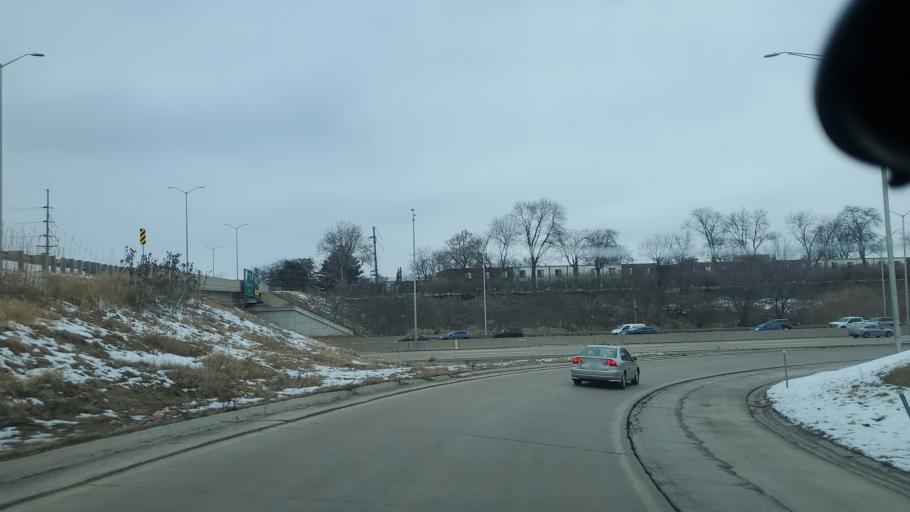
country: US
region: Illinois
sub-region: Kane County
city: North Aurora
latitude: 41.7950
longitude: -88.3273
